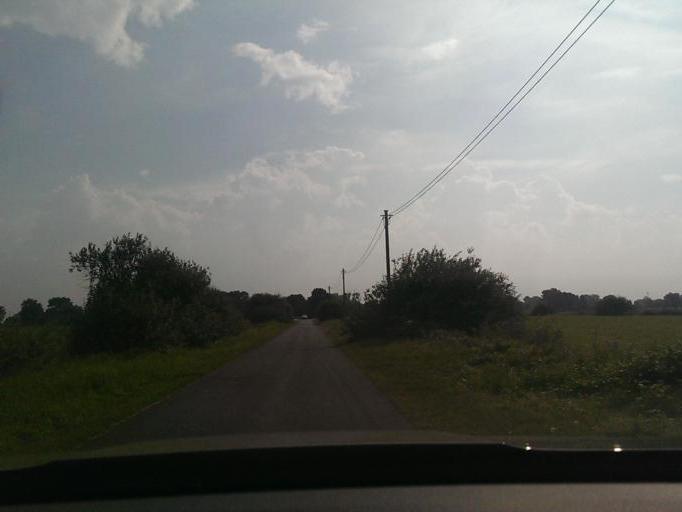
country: DE
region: Lower Saxony
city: Osterholz-Scharmbeck
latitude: 53.1679
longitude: 8.8022
